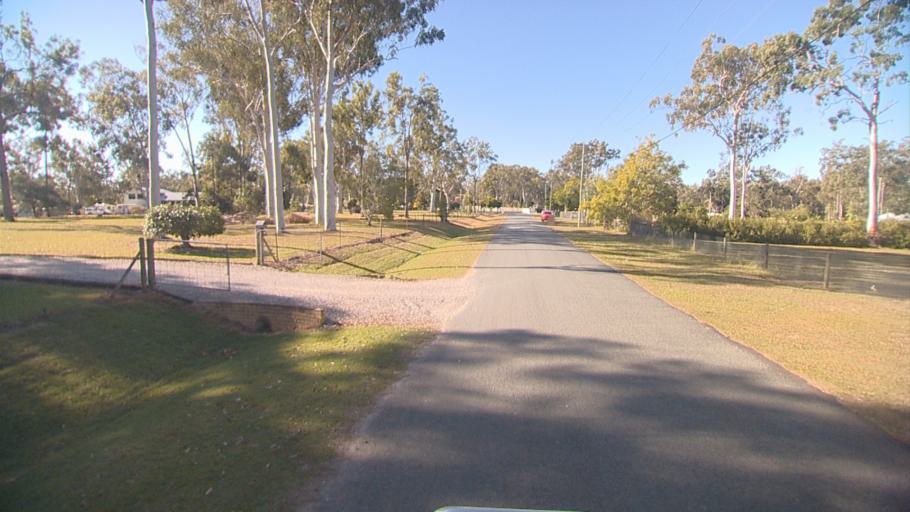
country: AU
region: Queensland
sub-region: Logan
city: Chambers Flat
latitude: -27.7360
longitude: 153.0666
